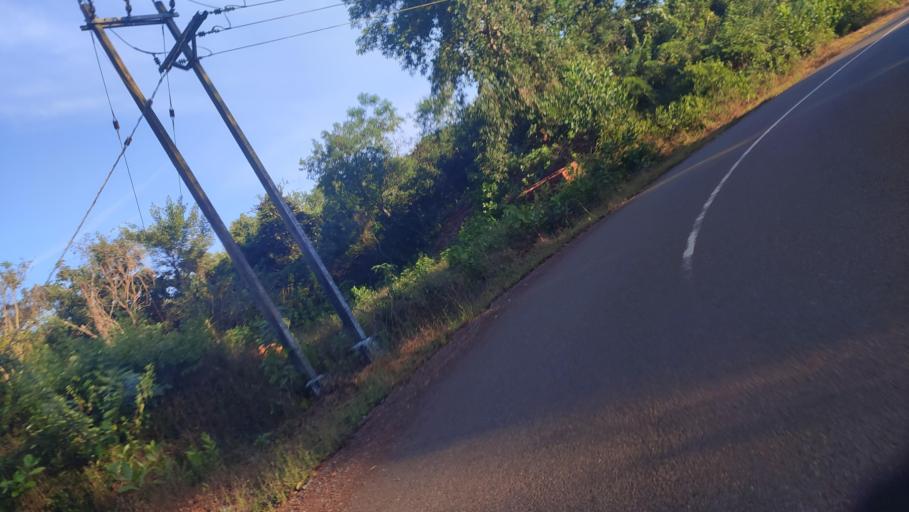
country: IN
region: Kerala
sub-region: Kasaragod District
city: Kasaragod
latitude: 12.4525
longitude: 75.0989
